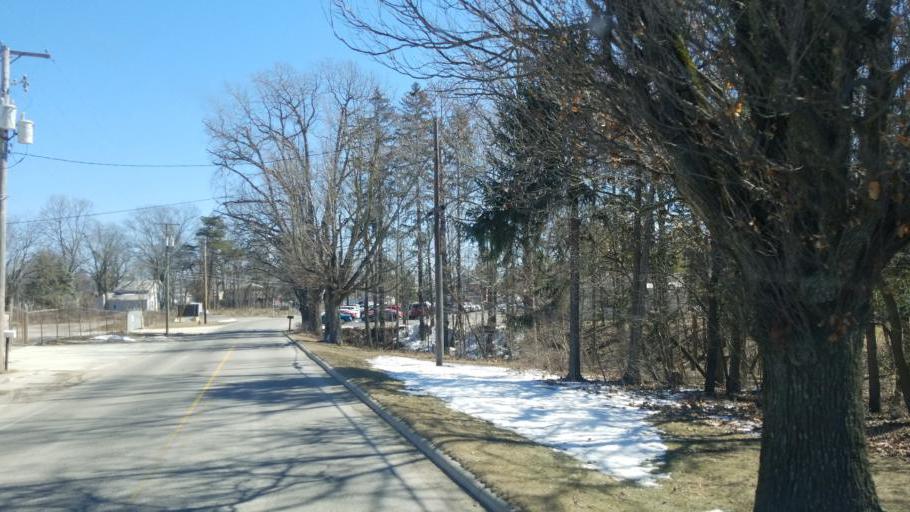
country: US
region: Ohio
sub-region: Crawford County
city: Bucyrus
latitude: 40.8094
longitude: -82.9866
